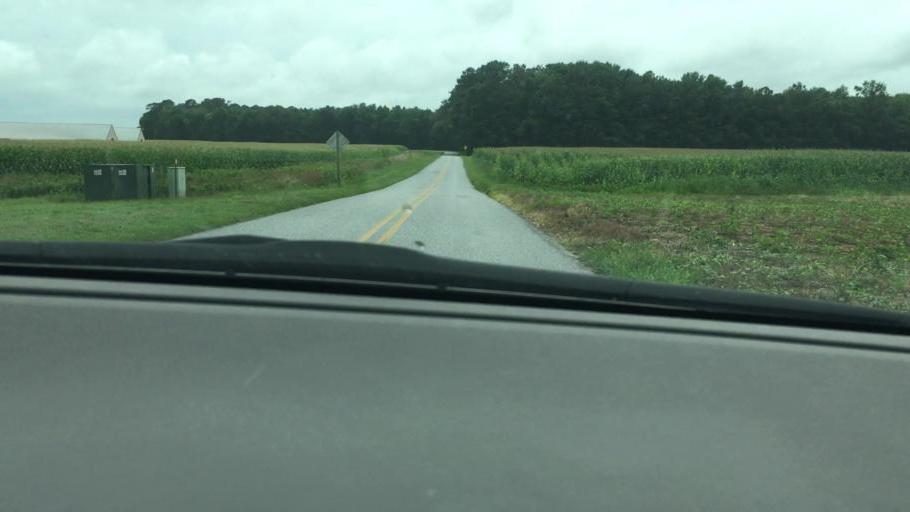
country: US
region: Maryland
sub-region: Worcester County
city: Pocomoke City
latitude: 38.0630
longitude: -75.5053
